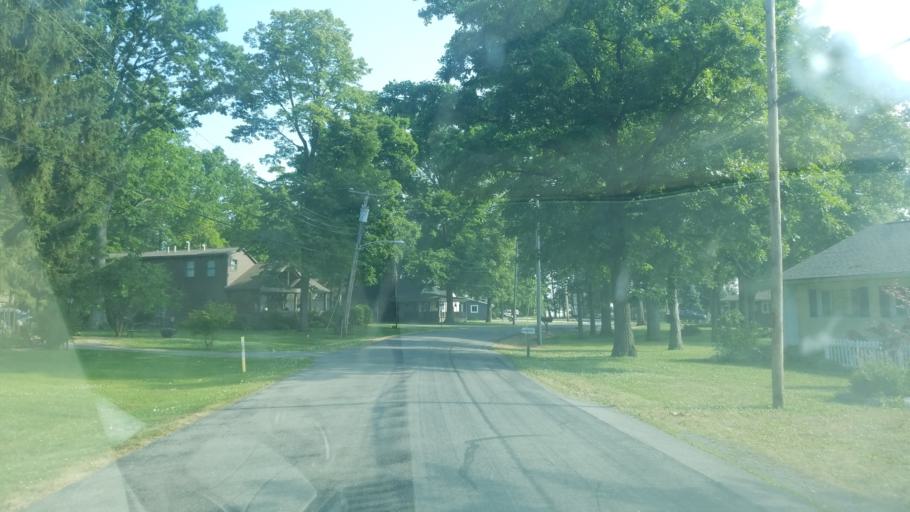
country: US
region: Ohio
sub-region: Logan County
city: Russells Point
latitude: 40.4995
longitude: -83.8695
